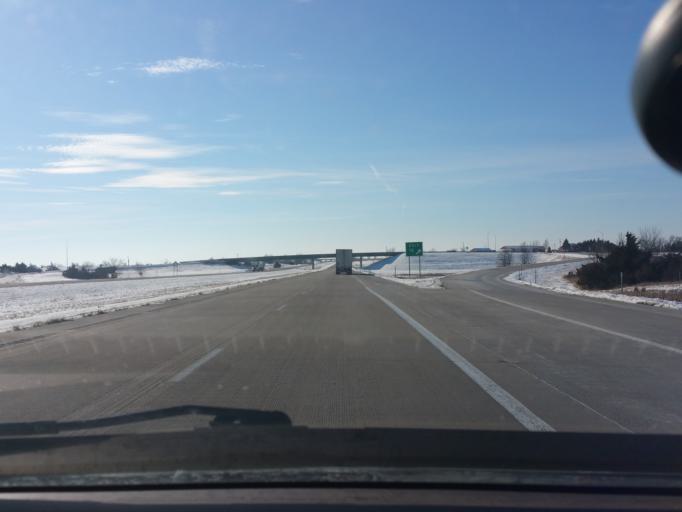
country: US
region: Iowa
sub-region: Decatur County
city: Leon
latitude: 40.8156
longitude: -93.8258
